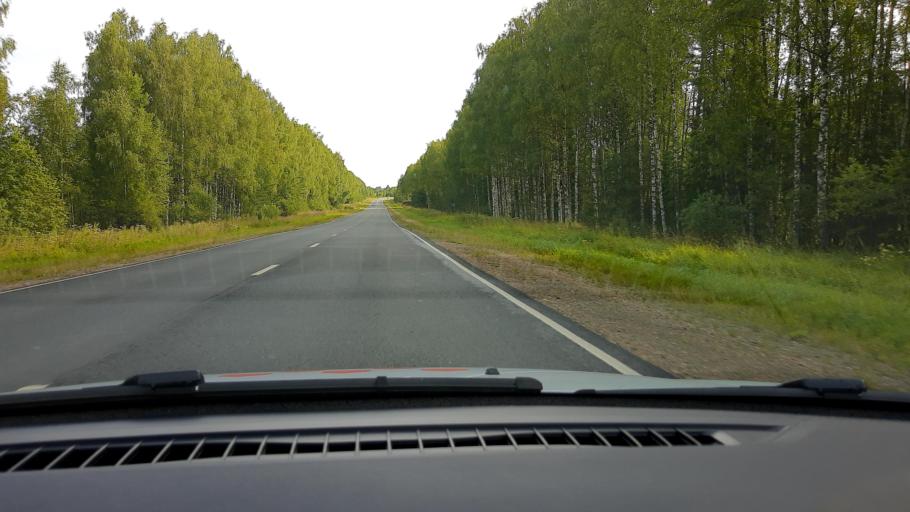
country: RU
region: Nizjnij Novgorod
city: Vladimirskoye
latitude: 56.9503
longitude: 45.0886
